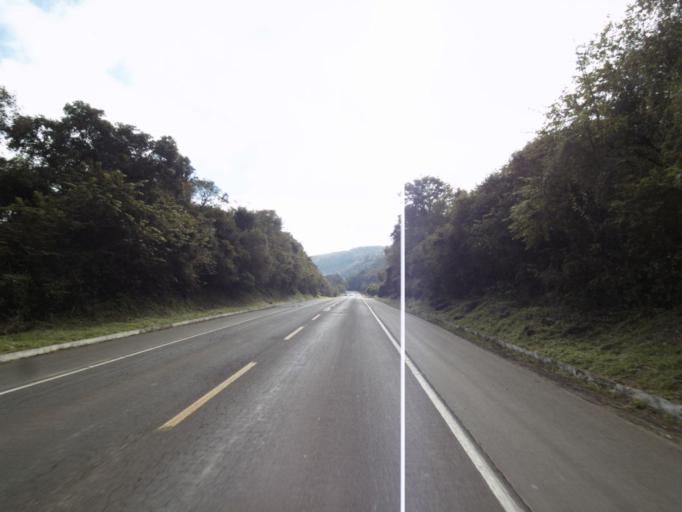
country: BR
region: Rio Grande do Sul
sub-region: Frederico Westphalen
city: Frederico Westphalen
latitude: -27.1496
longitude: -53.2143
